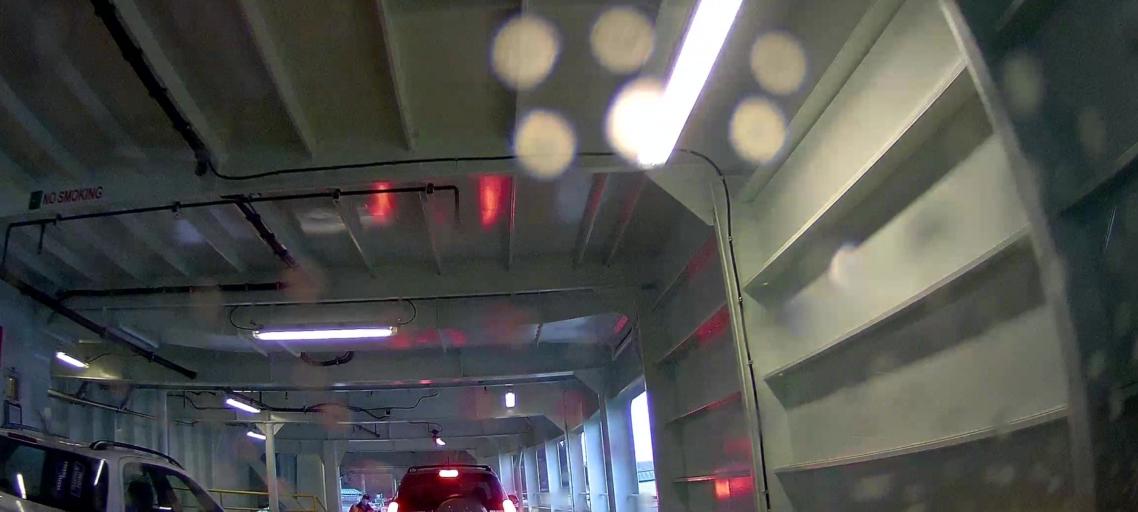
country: US
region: Washington
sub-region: Snohomish County
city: Mukilteo
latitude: 47.9744
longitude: -122.3486
